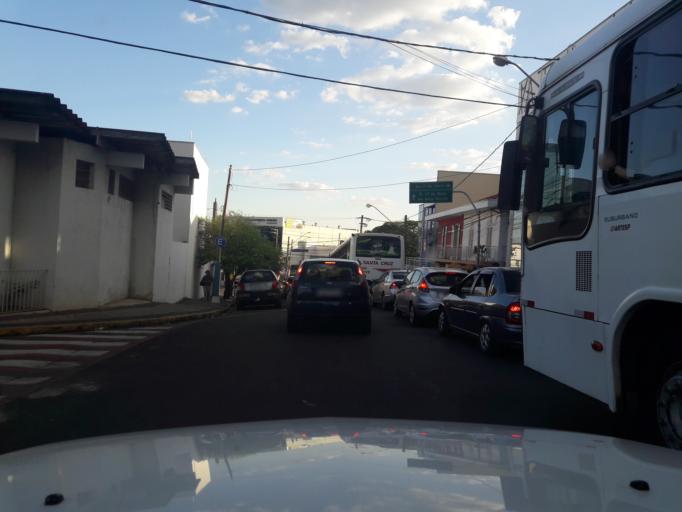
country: BR
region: Sao Paulo
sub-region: Moji-Guacu
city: Mogi-Gaucu
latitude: -22.3703
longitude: -46.9434
